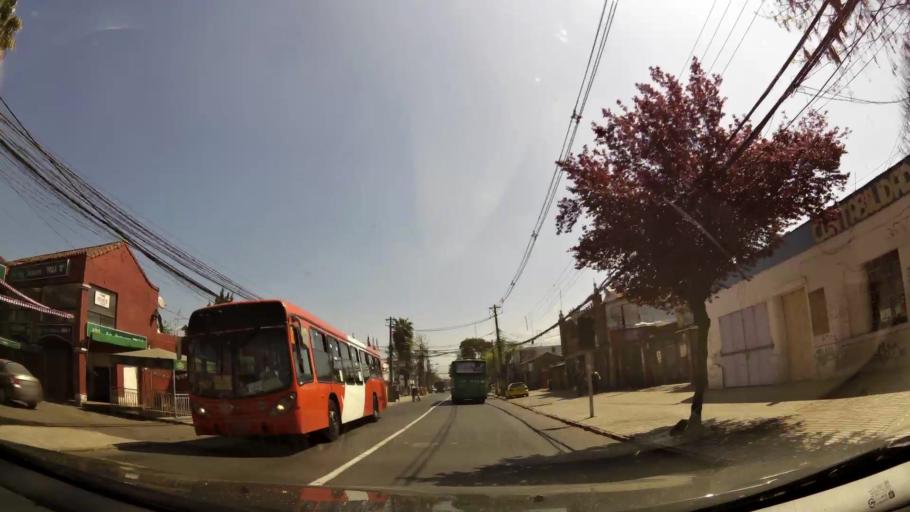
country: CL
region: Santiago Metropolitan
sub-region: Provincia de Santiago
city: Lo Prado
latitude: -33.3676
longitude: -70.7332
